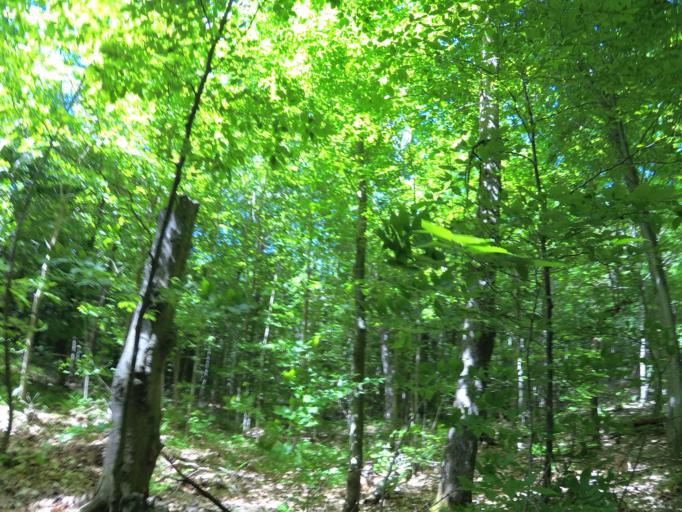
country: CA
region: Ontario
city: Renfrew
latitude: 45.0564
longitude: -76.8451
